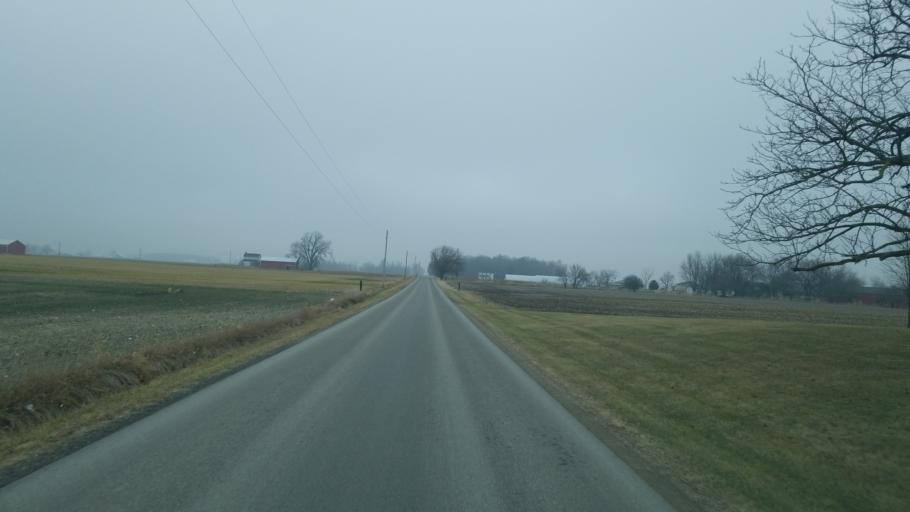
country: US
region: Indiana
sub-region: Adams County
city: Berne
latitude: 40.6660
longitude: -84.9943
